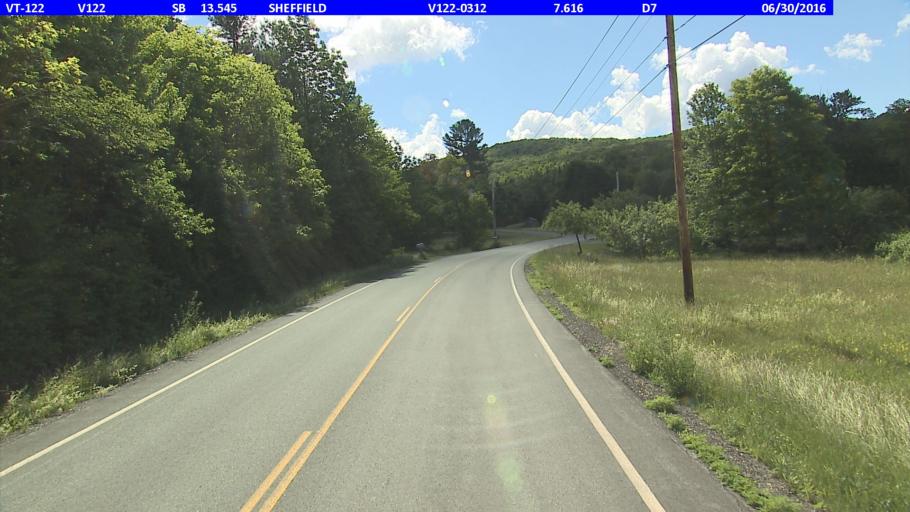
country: US
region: Vermont
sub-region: Caledonia County
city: Lyndonville
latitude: 44.6775
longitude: -72.1622
